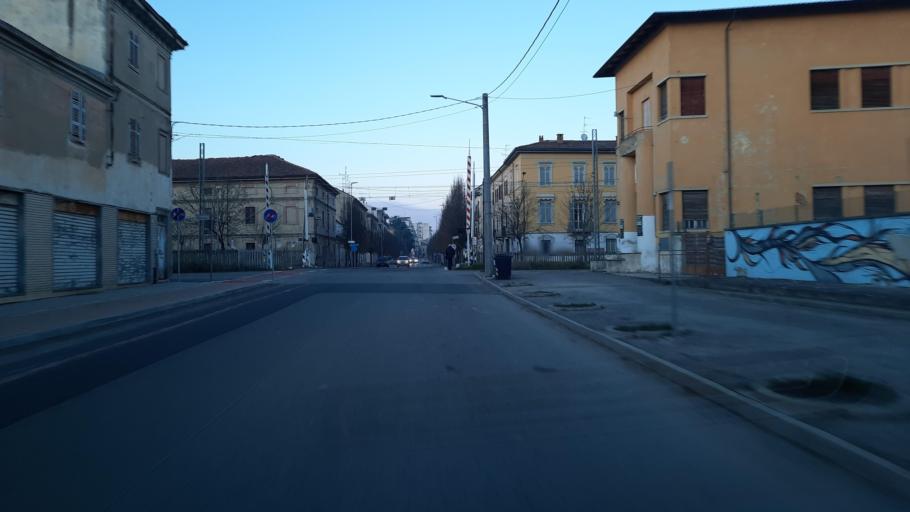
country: IT
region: Piedmont
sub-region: Provincia di Vercelli
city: Trino
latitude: 45.1893
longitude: 8.2962
